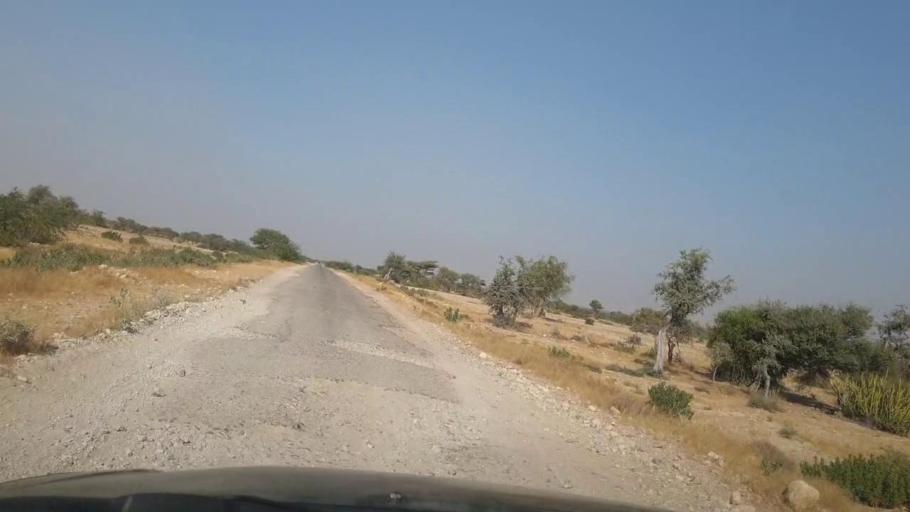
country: PK
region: Sindh
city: Jamshoro
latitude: 25.5440
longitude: 67.8265
